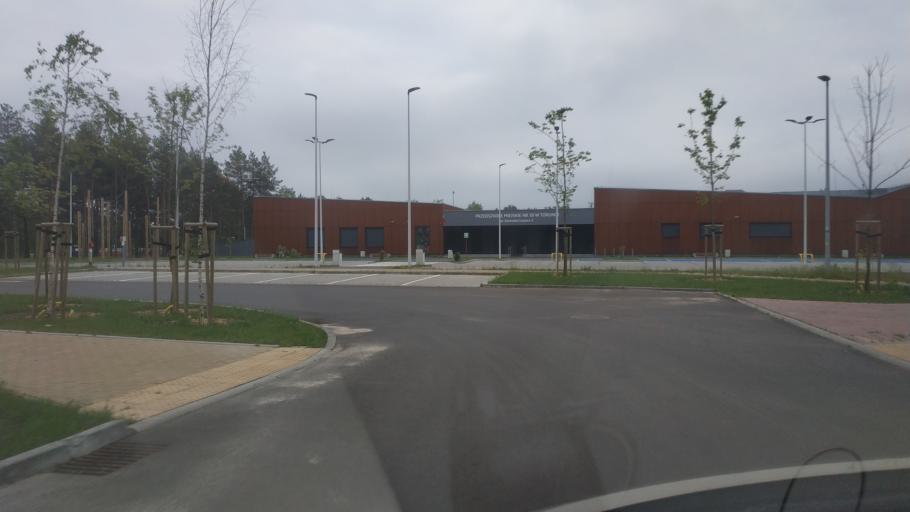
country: PL
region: Kujawsko-Pomorskie
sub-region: Torun
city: Torun
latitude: 53.0505
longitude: 18.6001
